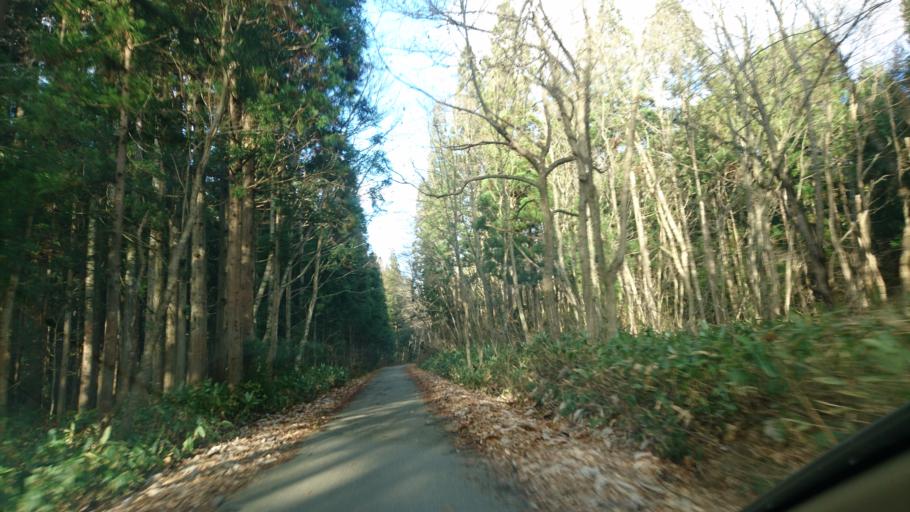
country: JP
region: Akita
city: Kakunodatemachi
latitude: 39.4644
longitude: 140.7892
